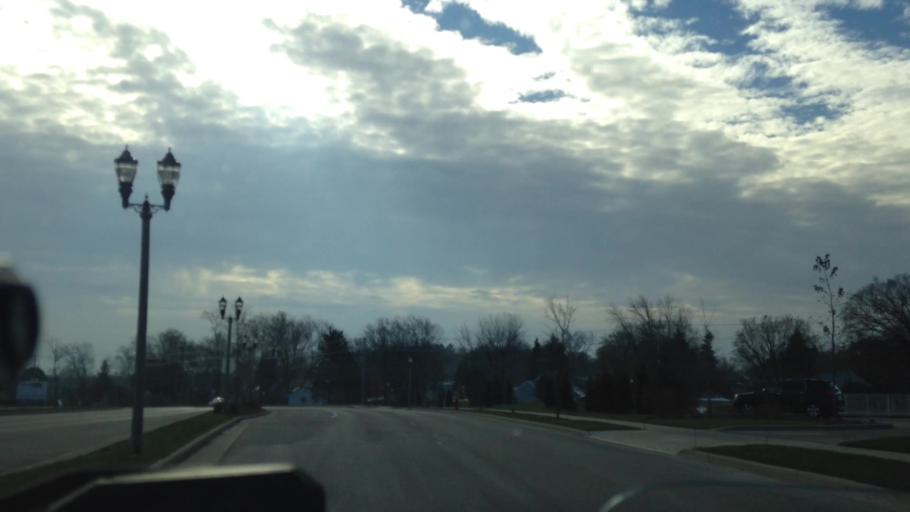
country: US
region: Wisconsin
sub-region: Waukesha County
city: Menomonee Falls
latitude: 43.1831
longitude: -88.1067
